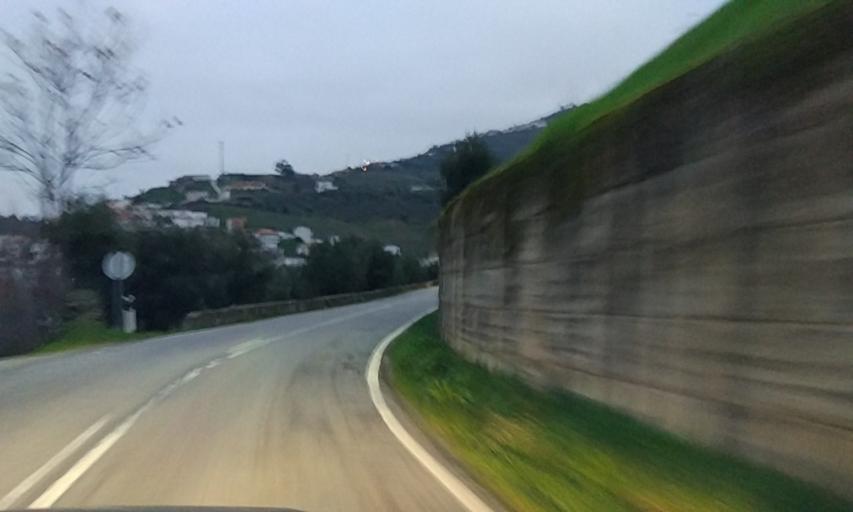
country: PT
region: Vila Real
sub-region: Sabrosa
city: Vilela
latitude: 41.1850
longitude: -7.5471
